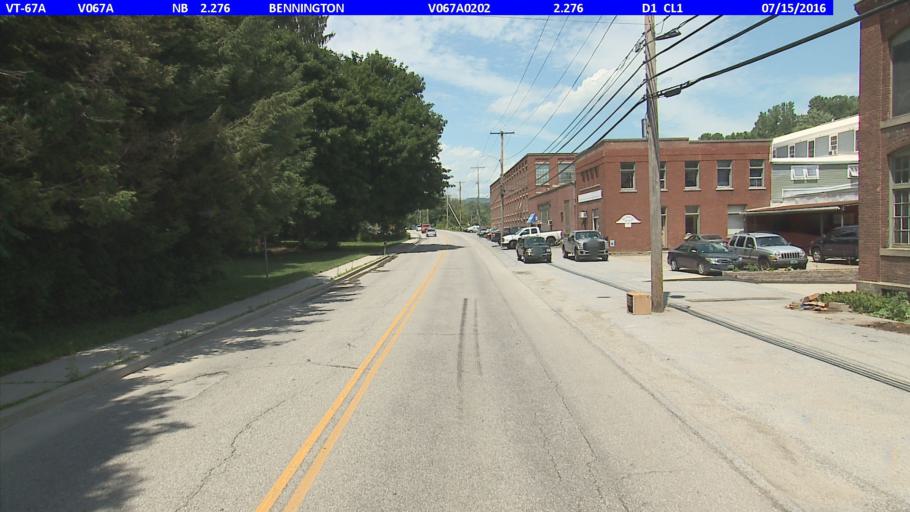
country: US
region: Vermont
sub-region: Bennington County
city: North Bennington
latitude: 42.9154
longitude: -73.2466
